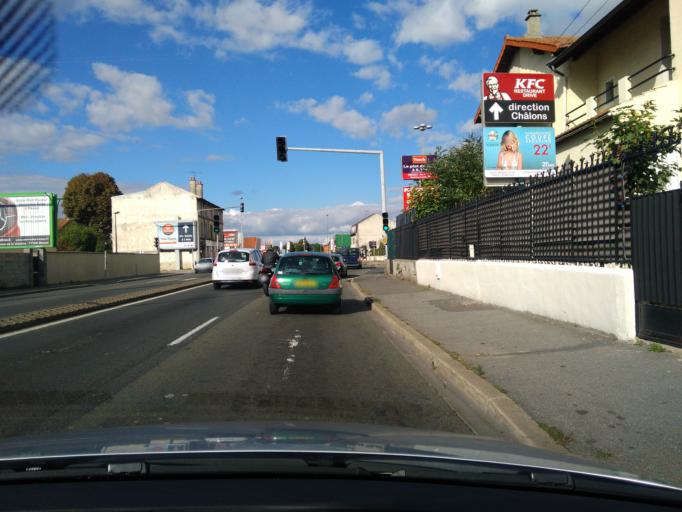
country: FR
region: Ile-de-France
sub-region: Departement de Seine-et-Marne
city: Meaux
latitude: 48.9456
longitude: 2.8796
